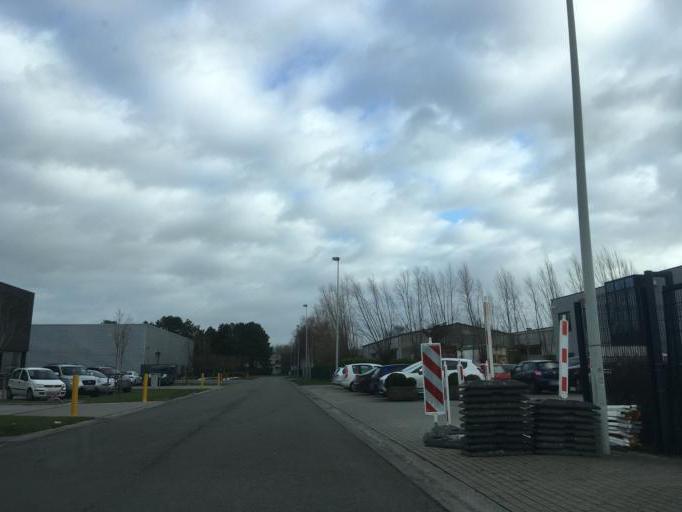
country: BE
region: Flanders
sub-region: Provincie West-Vlaanderen
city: Roeselare
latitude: 50.9758
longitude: 3.1279
